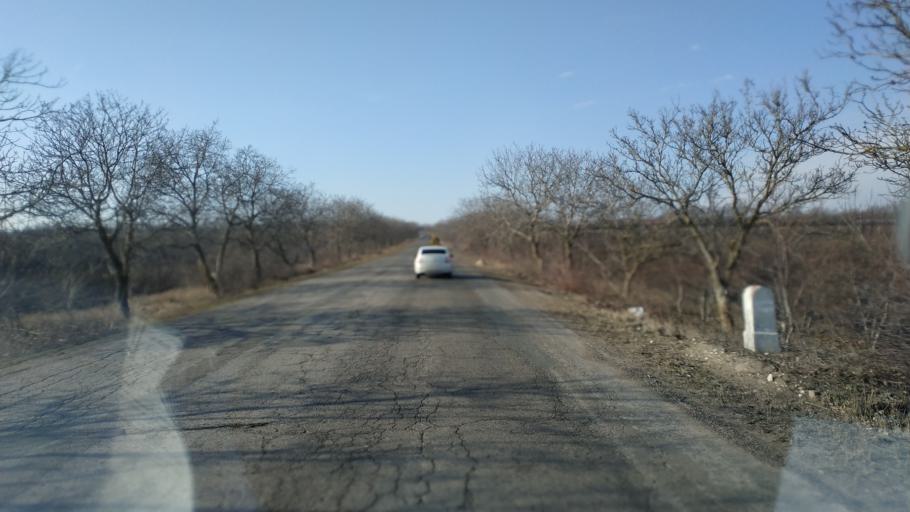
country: MD
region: Chisinau
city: Singera
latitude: 46.8667
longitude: 29.0374
